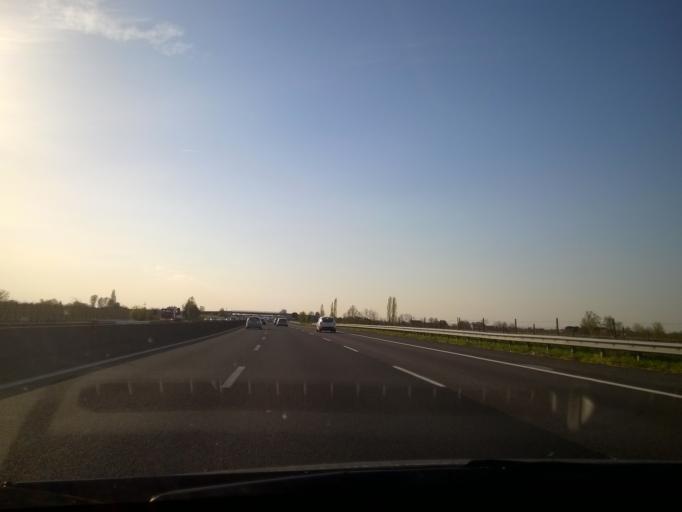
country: IT
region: Emilia-Romagna
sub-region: Provincia di Bologna
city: Castel Guelfo di Bologna
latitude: 44.3982
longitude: 11.6975
